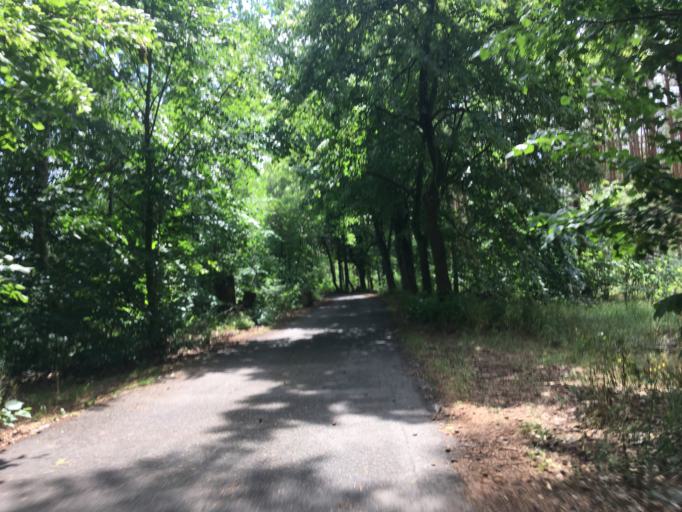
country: DE
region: Berlin
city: Schmockwitz
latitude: 52.3940
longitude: 13.6525
